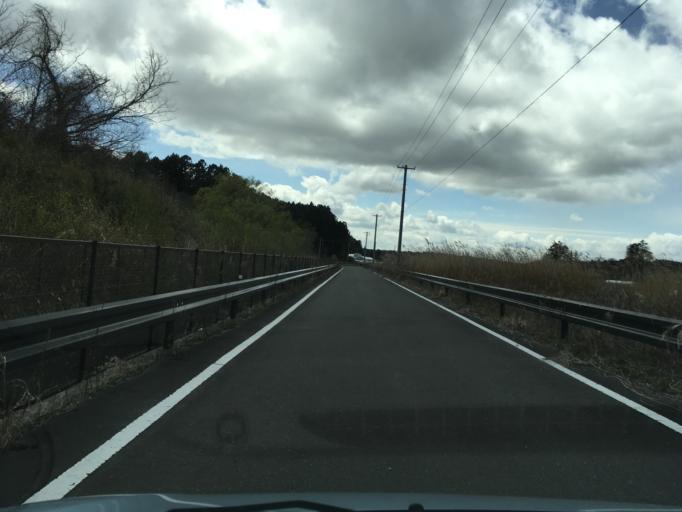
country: JP
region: Miyagi
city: Wakuya
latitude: 38.6811
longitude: 141.1049
